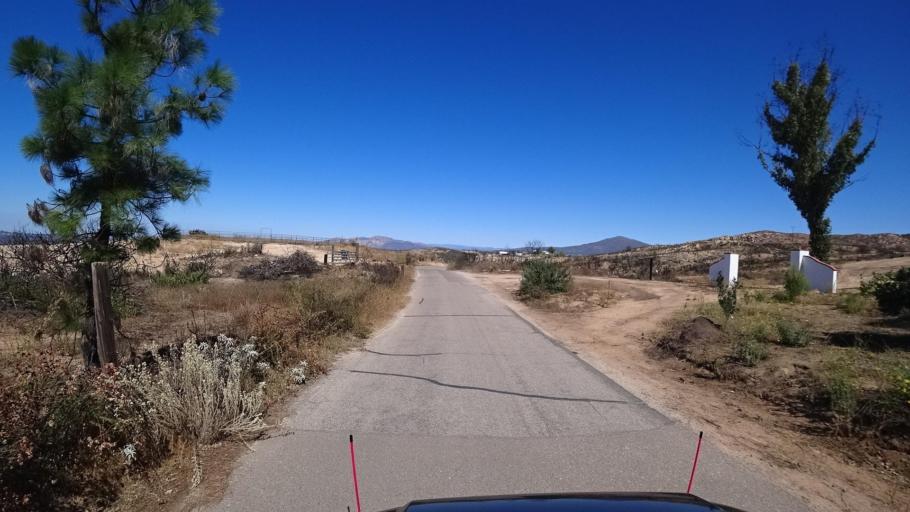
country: US
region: California
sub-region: San Diego County
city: Alpine
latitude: 32.7702
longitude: -116.7628
